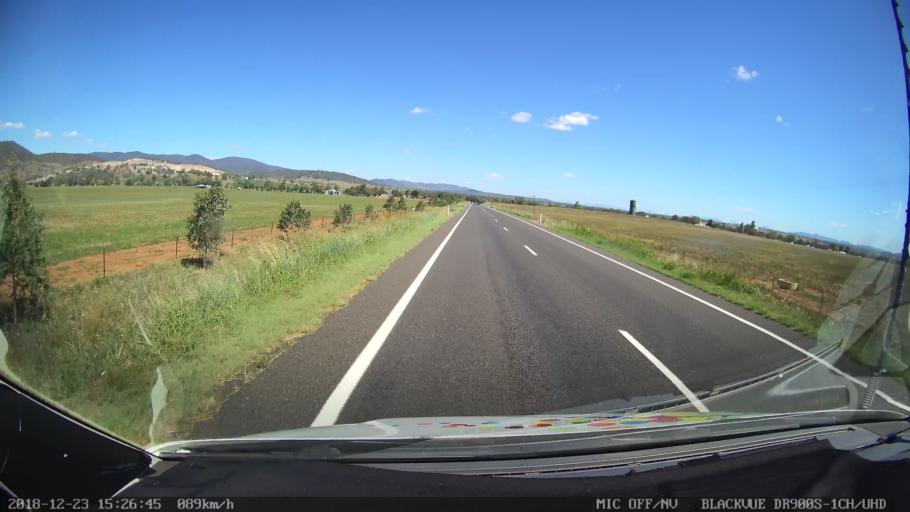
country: AU
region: New South Wales
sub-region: Tamworth Municipality
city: East Tamworth
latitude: -30.9206
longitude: 150.8408
